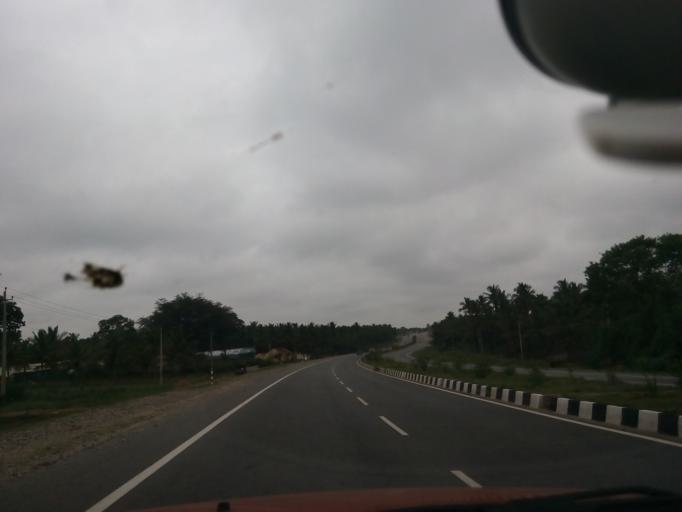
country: IN
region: Karnataka
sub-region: Hassan
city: Shravanabelagola
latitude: 12.9279
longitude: 76.5154
